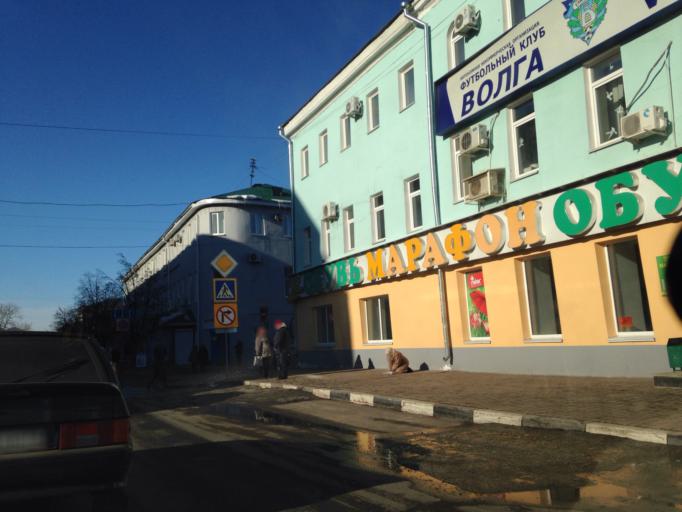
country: RU
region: Ulyanovsk
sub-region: Ulyanovskiy Rayon
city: Ulyanovsk
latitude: 54.3196
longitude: 48.3954
